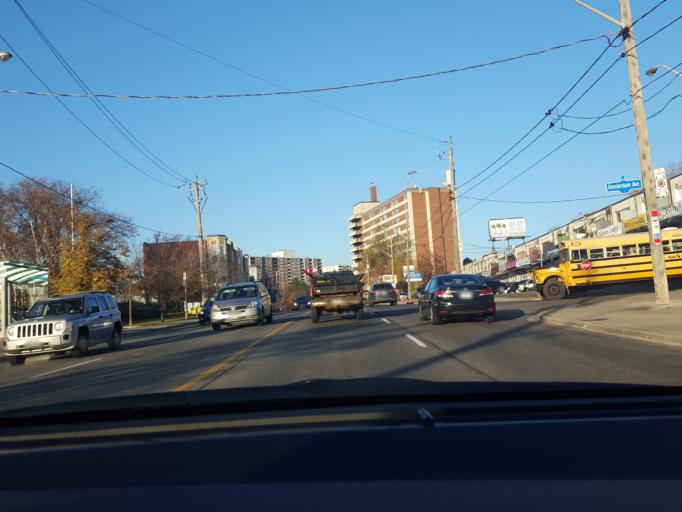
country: CA
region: Ontario
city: Scarborough
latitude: 43.7141
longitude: -79.3061
